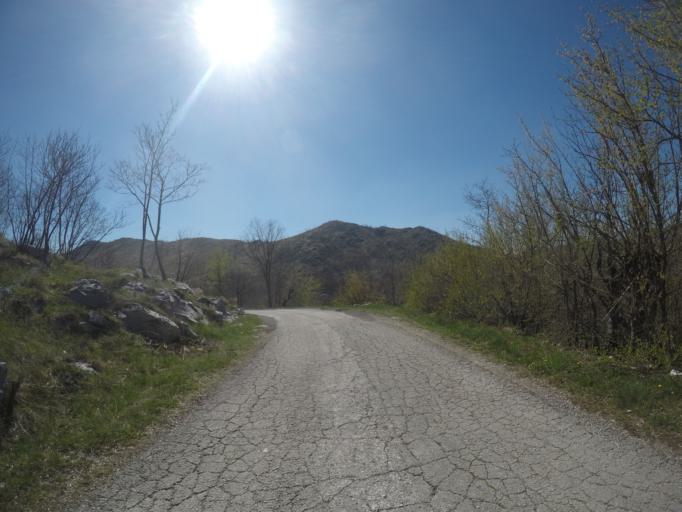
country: ME
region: Cetinje
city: Cetinje
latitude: 42.5374
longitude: 18.9832
